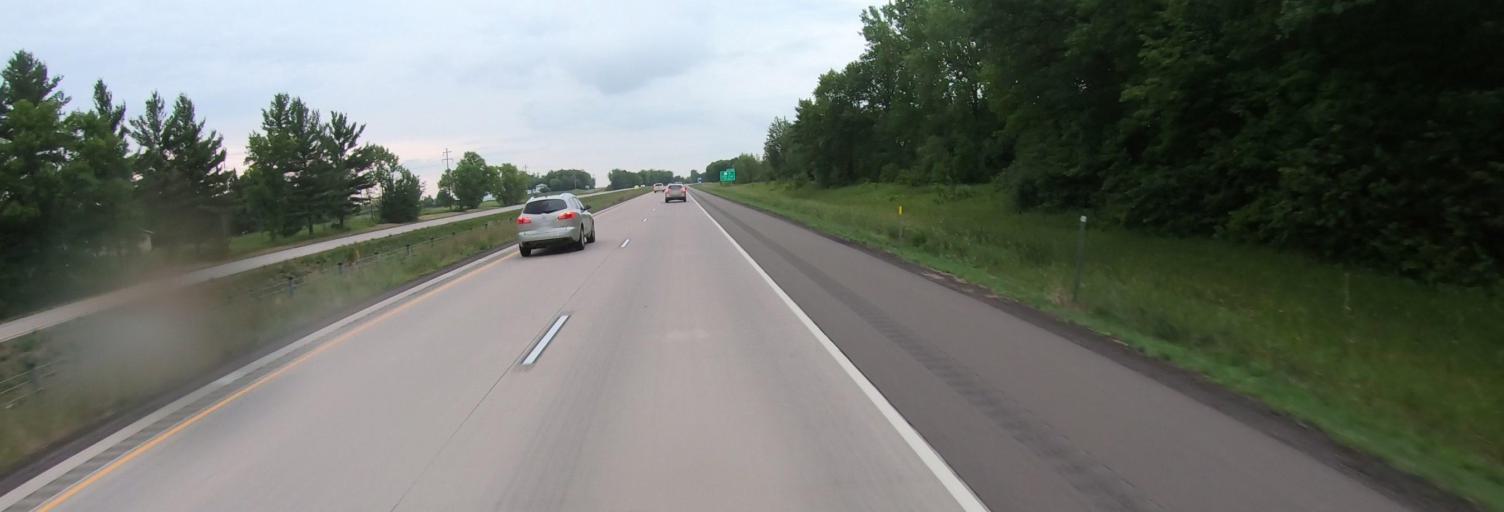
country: US
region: Minnesota
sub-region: Pine County
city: Pine City
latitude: 45.7976
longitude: -92.9901
